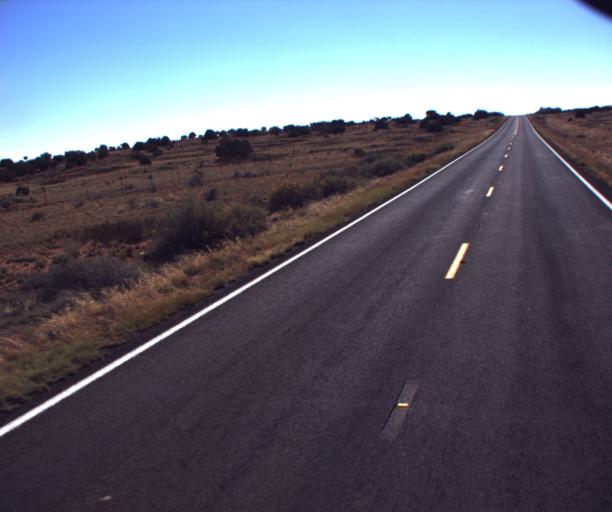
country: US
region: Arizona
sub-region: Coconino County
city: Tuba City
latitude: 35.9254
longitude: -110.8562
